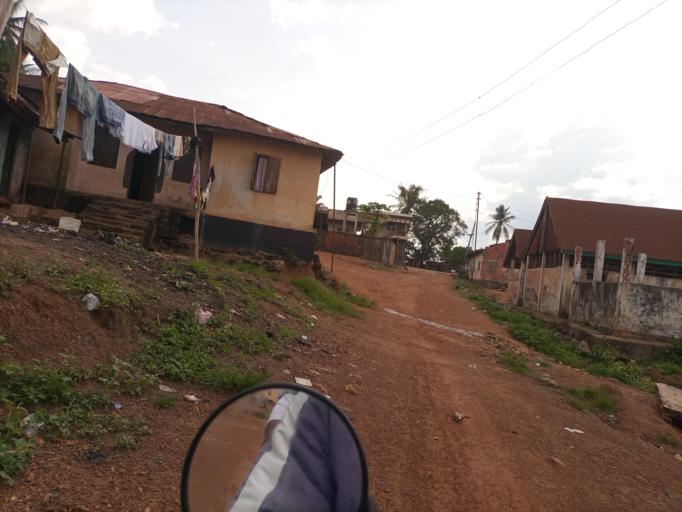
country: SL
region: Southern Province
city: Bo
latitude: 7.9593
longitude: -11.7324
